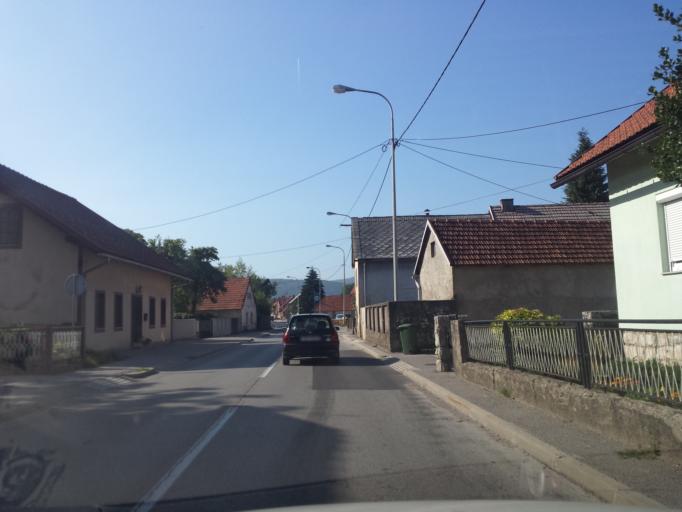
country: HR
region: Karlovacka
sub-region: Grad Ogulin
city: Ogulin
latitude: 45.2610
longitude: 15.2339
